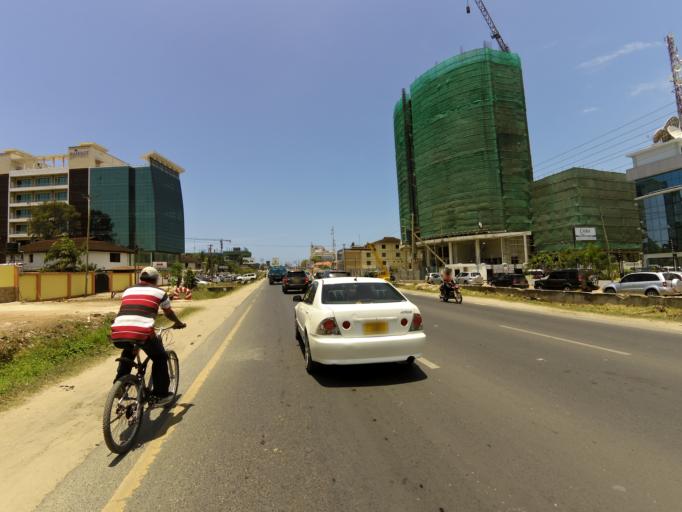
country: TZ
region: Dar es Salaam
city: Magomeni
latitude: -6.7778
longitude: 39.2594
